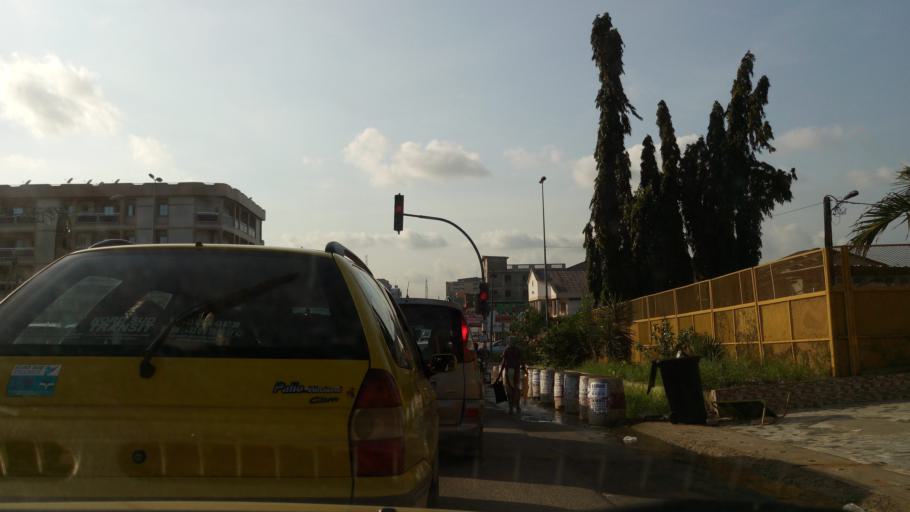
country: CI
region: Lagunes
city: Abobo
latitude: 5.3923
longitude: -3.9760
